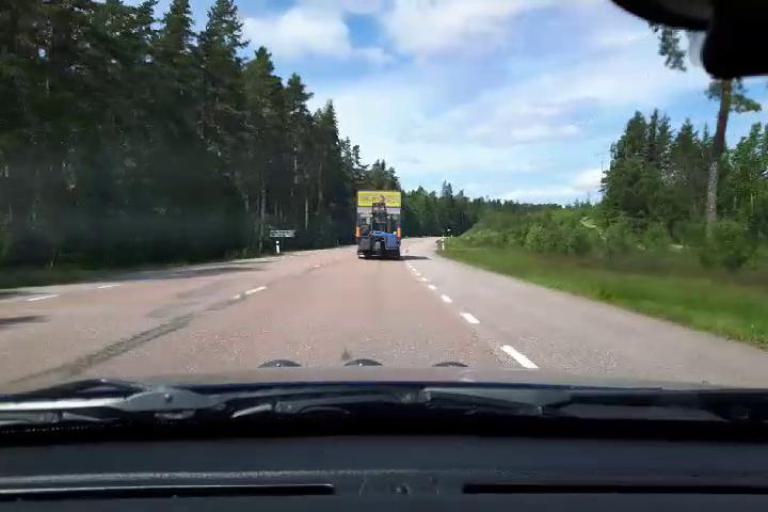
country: SE
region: Uppsala
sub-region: Osthammars Kommun
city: Bjorklinge
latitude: 60.1216
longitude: 17.5106
